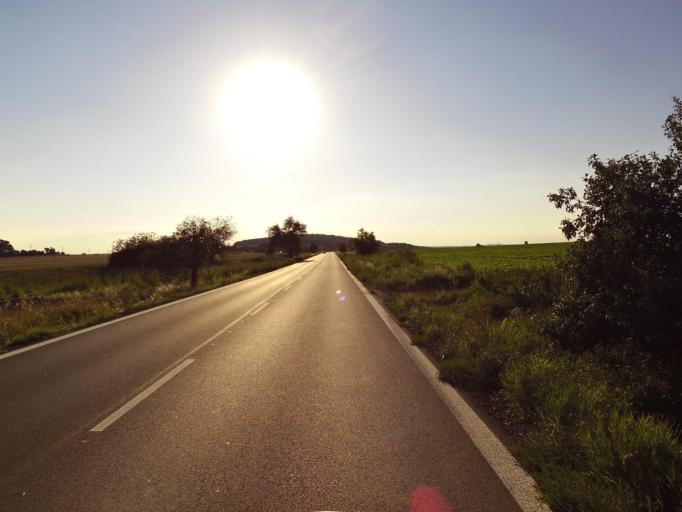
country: CZ
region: Central Bohemia
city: Knezmost
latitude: 50.5073
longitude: 15.0170
